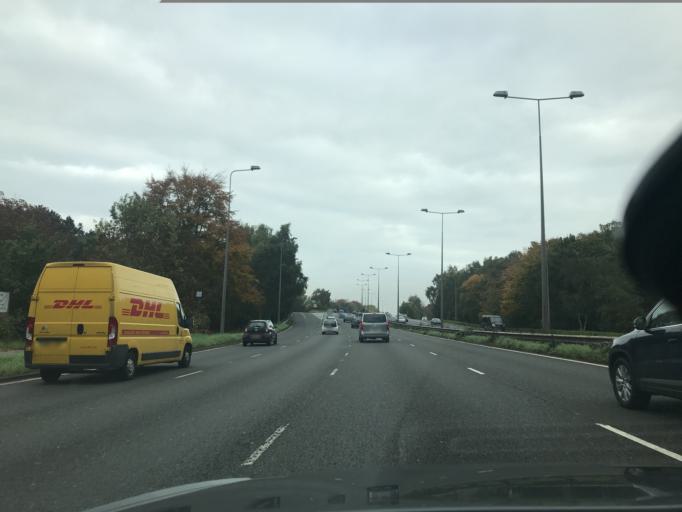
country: GB
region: England
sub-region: Manchester
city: Chorlton cum Hardy
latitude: 53.4035
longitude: -2.2677
